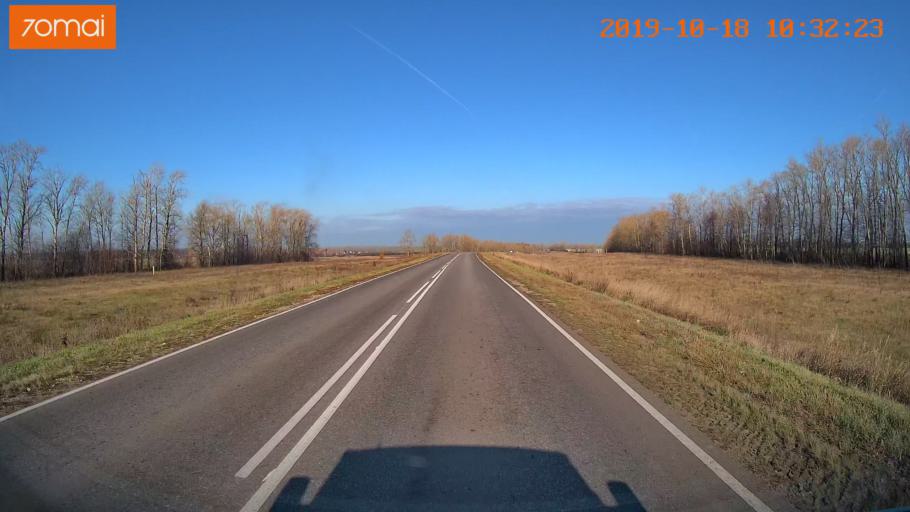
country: RU
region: Tula
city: Kurkino
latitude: 53.4934
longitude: 38.6233
